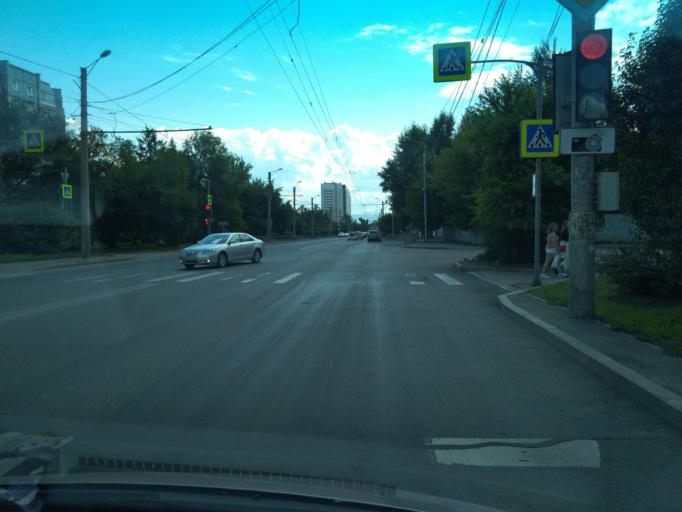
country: RU
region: Krasnoyarskiy
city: Solnechnyy
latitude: 56.0459
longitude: 92.9413
